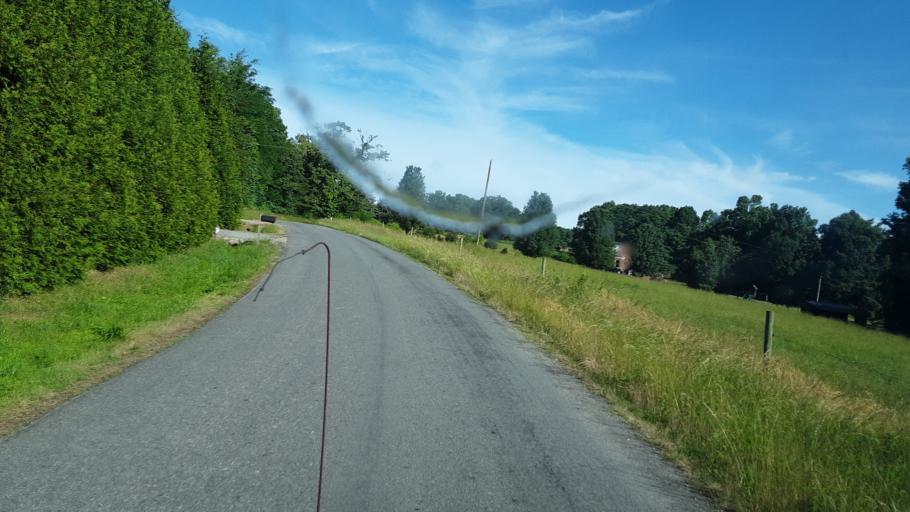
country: US
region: Virginia
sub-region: Pittsylvania County
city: Chatham
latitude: 36.8400
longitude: -79.4138
